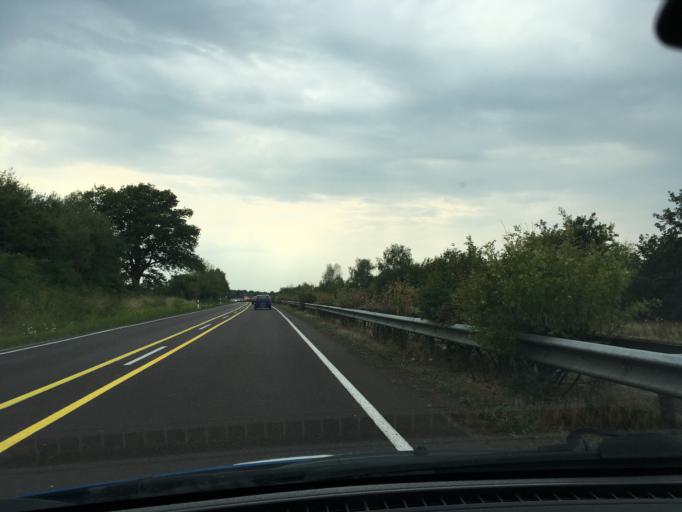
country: DE
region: Lower Saxony
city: Burgdorf
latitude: 52.4693
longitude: 9.9659
